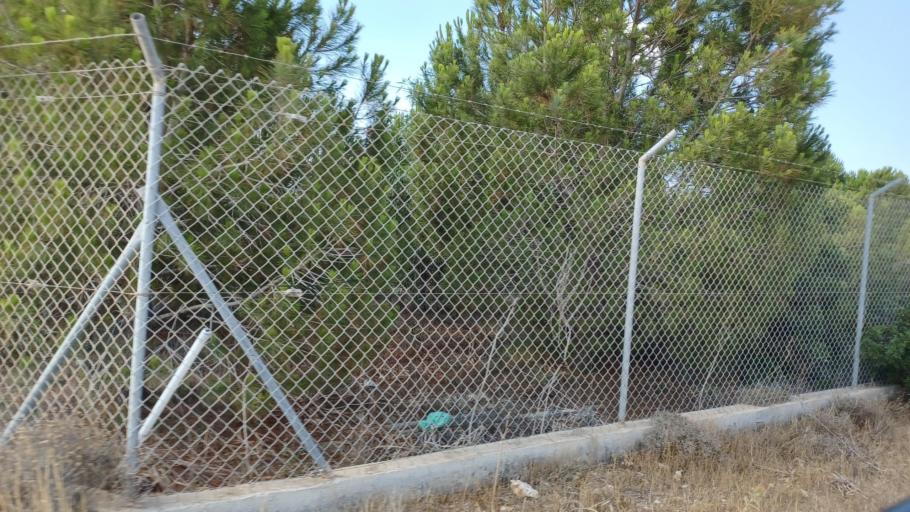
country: CY
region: Ammochostos
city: Deryneia
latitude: 35.0684
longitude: 33.9677
